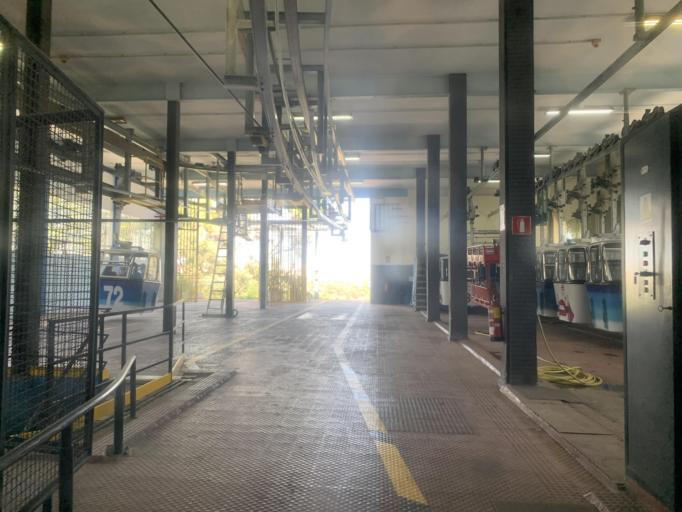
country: ES
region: Madrid
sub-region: Provincia de Madrid
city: Moncloa-Aravaca
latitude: 40.4196
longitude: -3.7486
